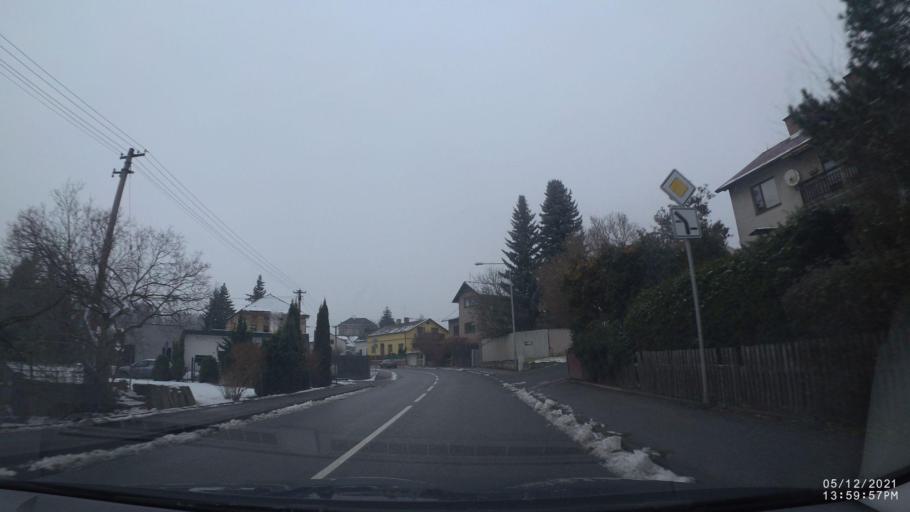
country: CZ
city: Hronov
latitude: 50.4806
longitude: 16.1710
